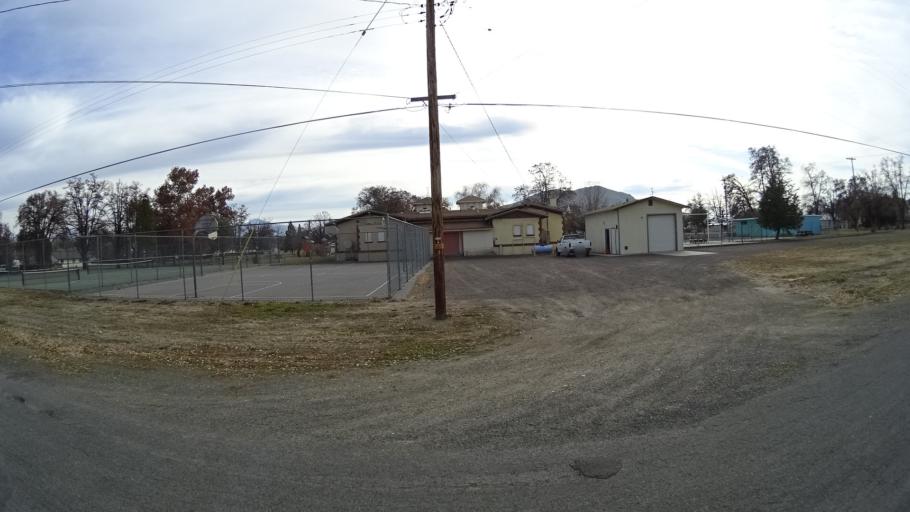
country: US
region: California
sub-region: Siskiyou County
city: Montague
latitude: 41.7280
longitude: -122.5328
